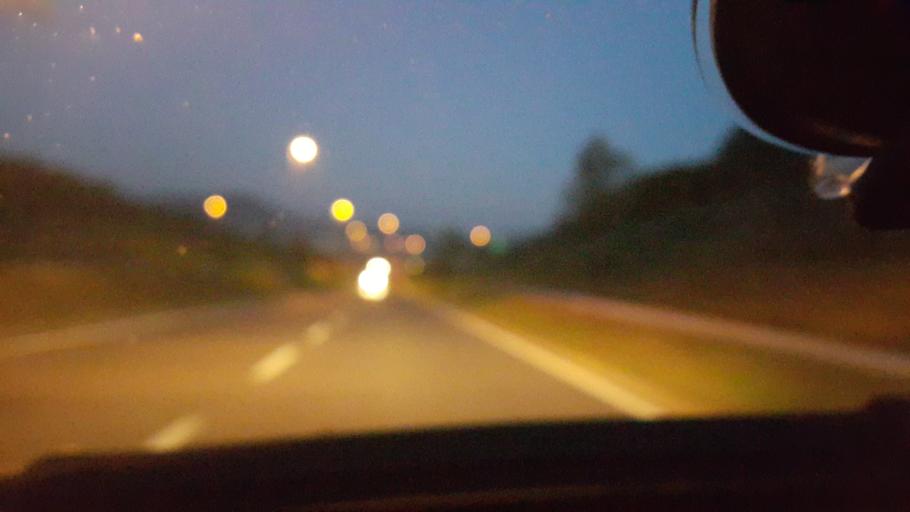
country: SI
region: Miklavz na Dravskem Polju
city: Miklavz na Dravskem Polju
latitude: 46.5434
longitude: 15.6943
